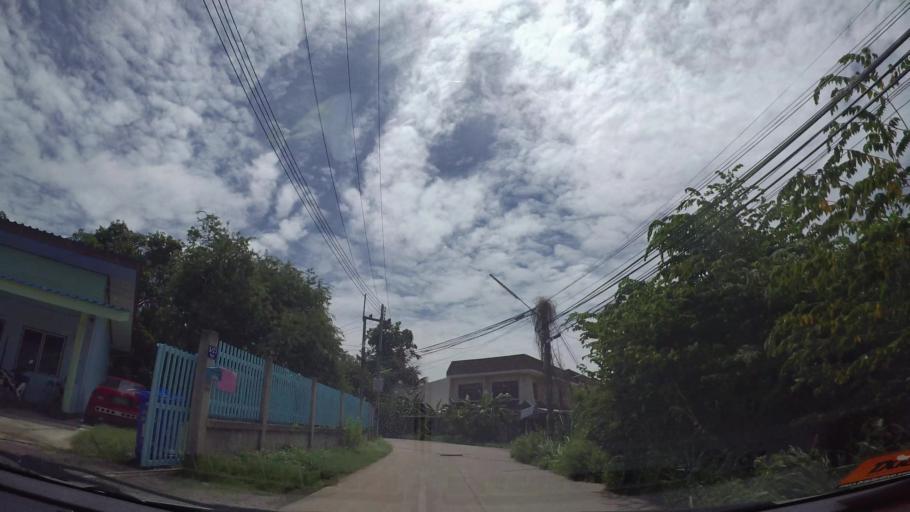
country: TH
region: Chon Buri
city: Sattahip
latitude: 12.7030
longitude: 100.8879
